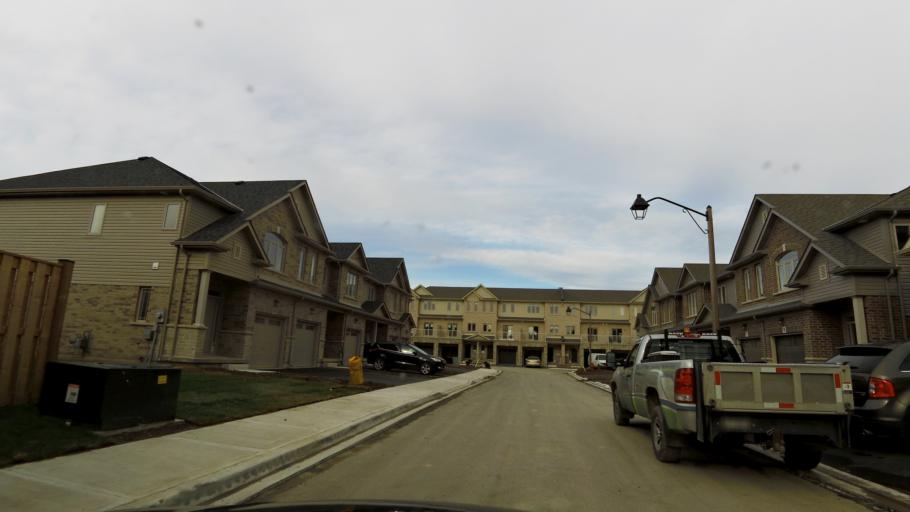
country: CA
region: Ontario
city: Hamilton
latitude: 43.1763
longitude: -79.7946
